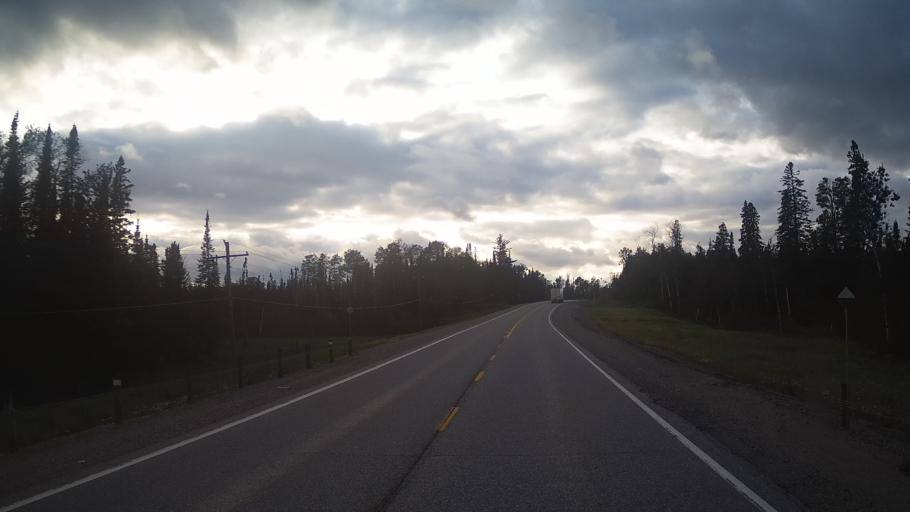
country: CA
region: Ontario
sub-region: Rainy River District
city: Atikokan
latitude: 49.0158
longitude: -90.4342
